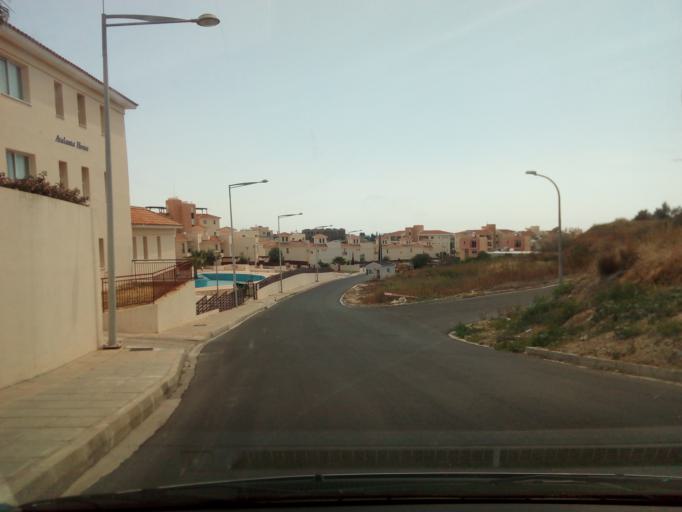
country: CY
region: Pafos
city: Chlorakas
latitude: 34.7913
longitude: 32.4173
